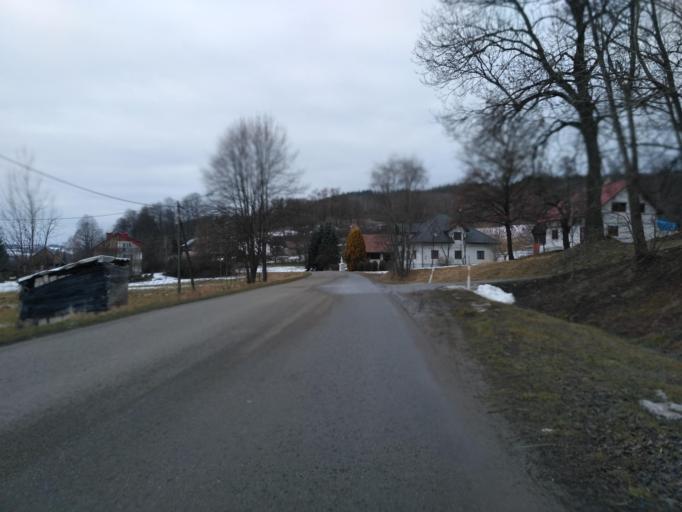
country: PL
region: Subcarpathian Voivodeship
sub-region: Powiat brzozowski
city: Wesola
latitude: 49.7761
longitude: 22.1438
